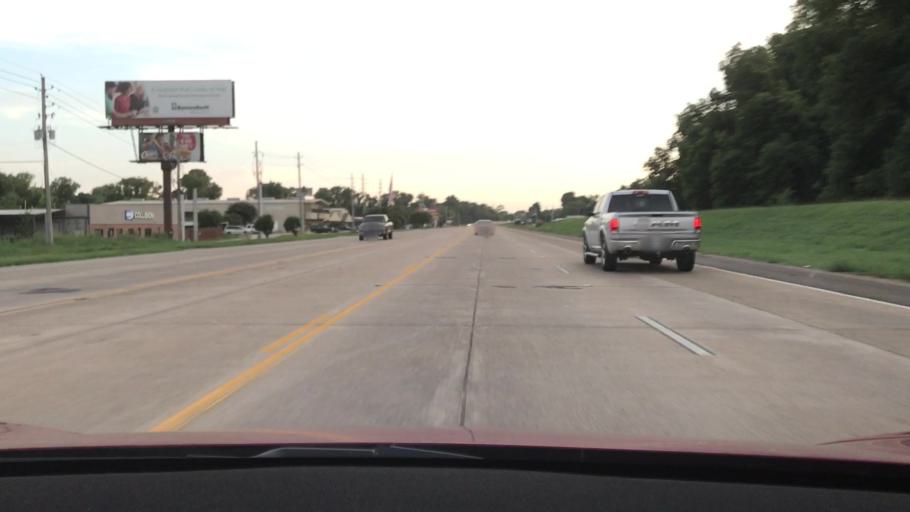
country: US
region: Louisiana
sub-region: Bossier Parish
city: Bossier City
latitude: 32.4538
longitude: -93.6942
